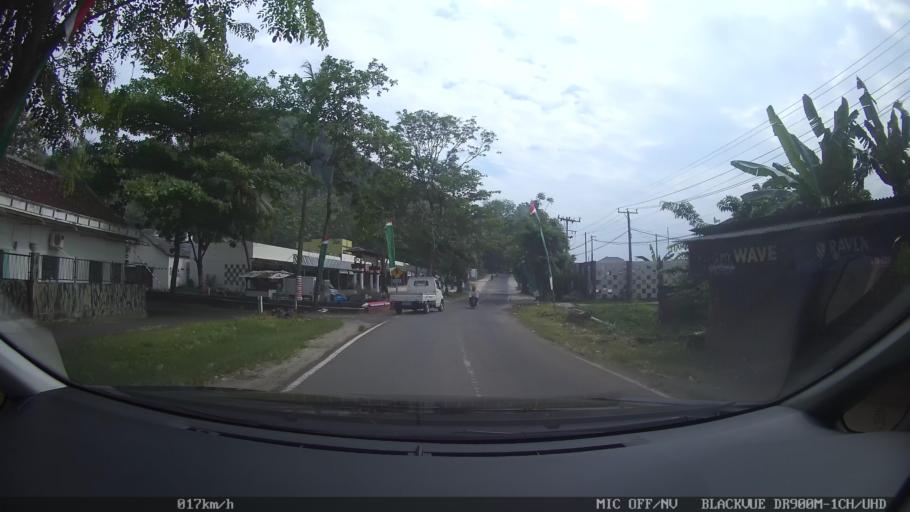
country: ID
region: Lampung
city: Bandarlampung
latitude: -5.4619
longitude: 105.2433
